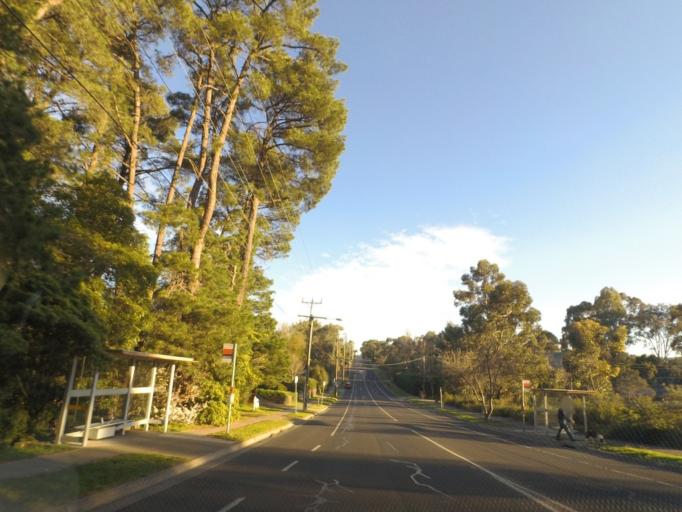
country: AU
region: Victoria
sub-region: Maroondah
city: Warranwood
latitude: -37.7830
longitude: 145.2489
